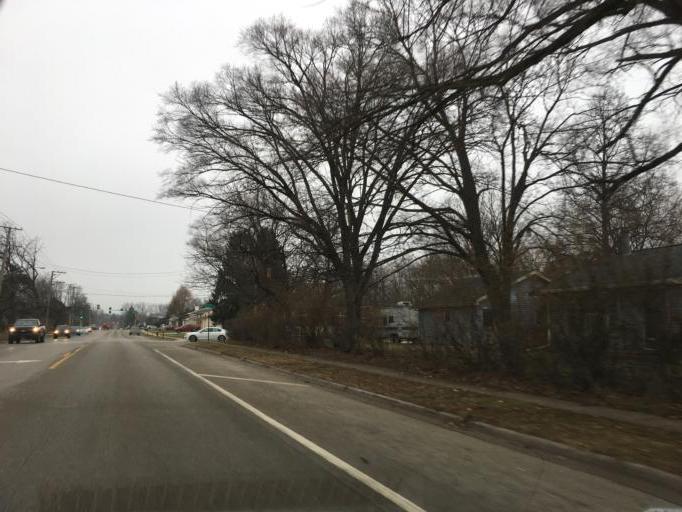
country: US
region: Illinois
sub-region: McHenry County
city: Lakewood
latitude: 42.2233
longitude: -88.3379
